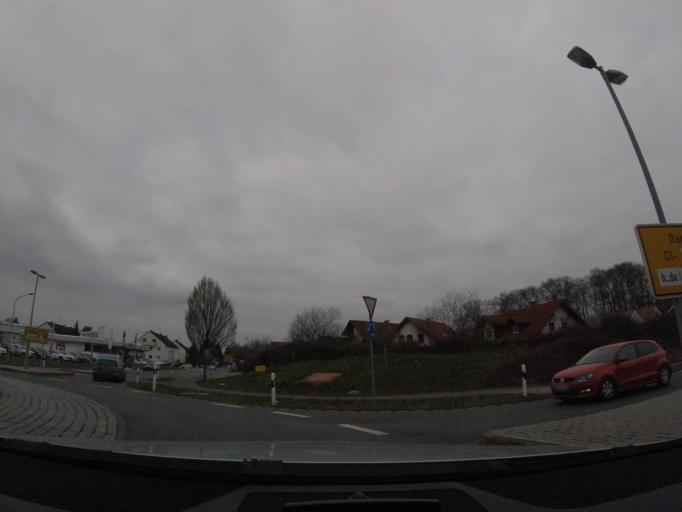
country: DE
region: Hesse
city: Dieburg
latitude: 49.8935
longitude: 8.8575
